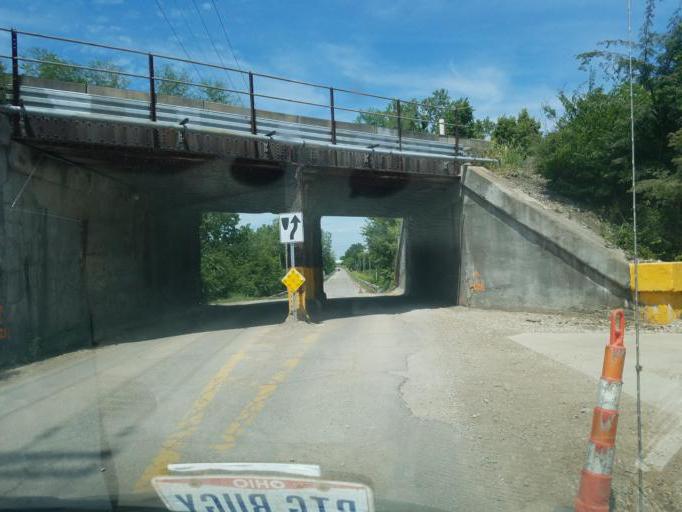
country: US
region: Ohio
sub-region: Madison County
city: West Jefferson
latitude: 39.9467
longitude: -83.2690
